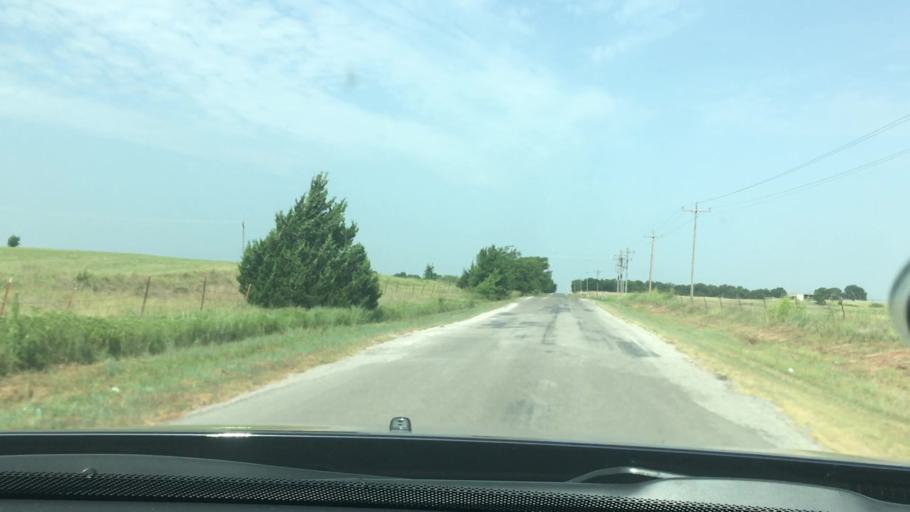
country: US
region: Oklahoma
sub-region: Garvin County
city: Pauls Valley
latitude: 34.7966
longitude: -97.1624
